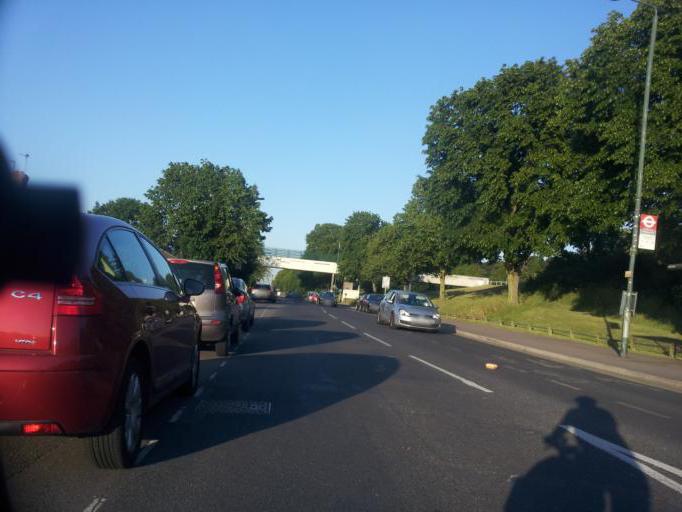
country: GB
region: England
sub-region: Greater London
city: Abbey Wood
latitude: 51.4900
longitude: 0.1265
